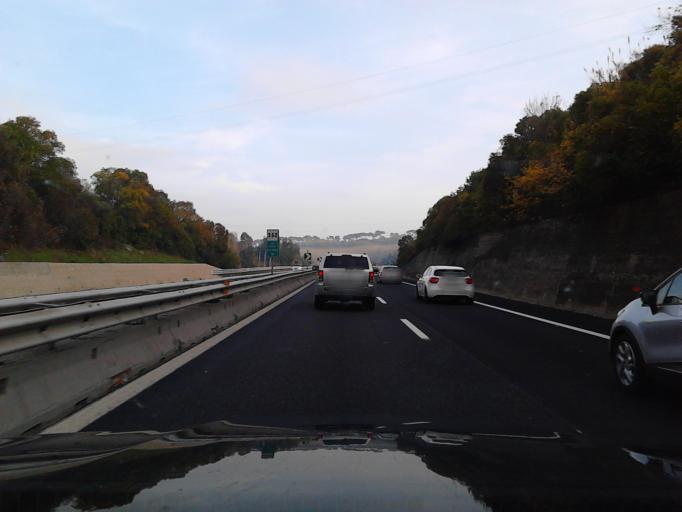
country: IT
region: Abruzzo
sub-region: Provincia di Teramo
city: Borgo Santa Maria Immacolata
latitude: 42.6046
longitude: 14.0551
